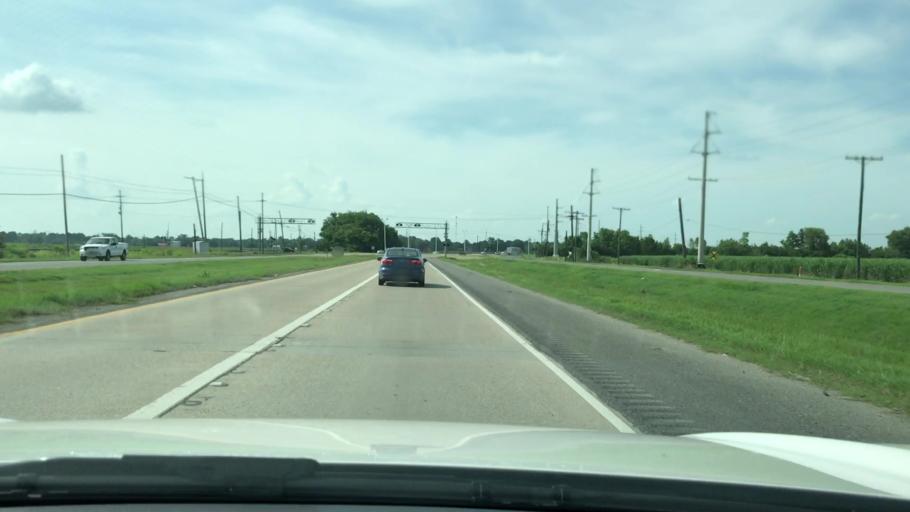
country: US
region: Louisiana
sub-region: West Baton Rouge Parish
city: Addis
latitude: 30.3381
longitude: -91.2594
